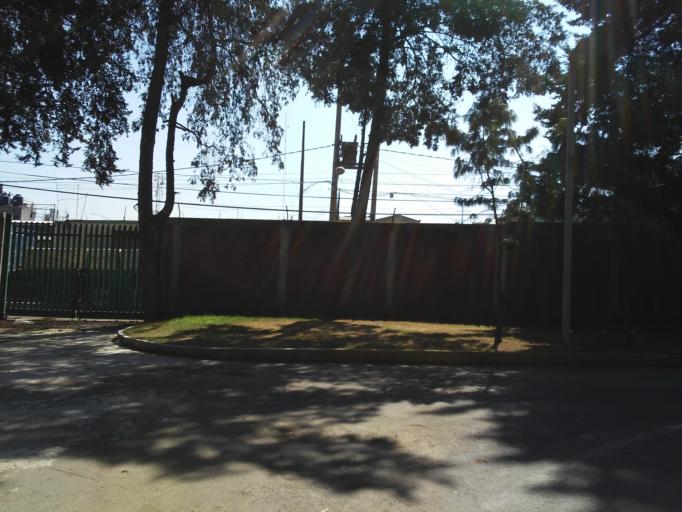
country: MX
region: Mexico
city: Toluca
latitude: 19.2716
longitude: -99.6493
